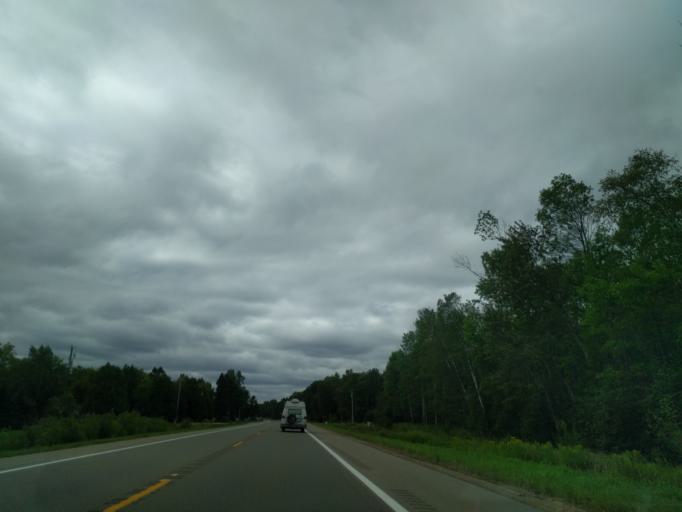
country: US
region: Michigan
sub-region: Menominee County
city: Menominee
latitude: 45.2314
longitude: -87.5081
